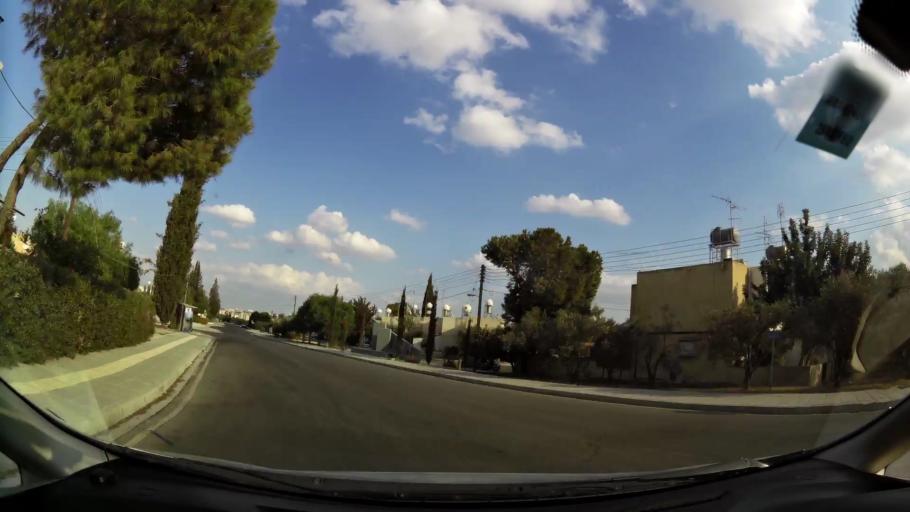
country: CY
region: Lefkosia
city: Kato Deftera
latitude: 35.1027
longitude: 33.2882
